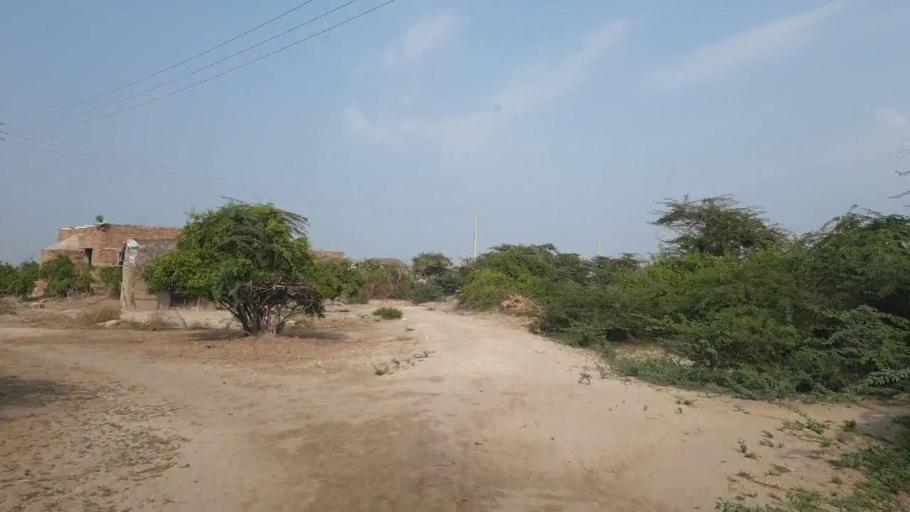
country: PK
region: Sindh
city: Kadhan
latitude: 24.4568
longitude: 68.8144
